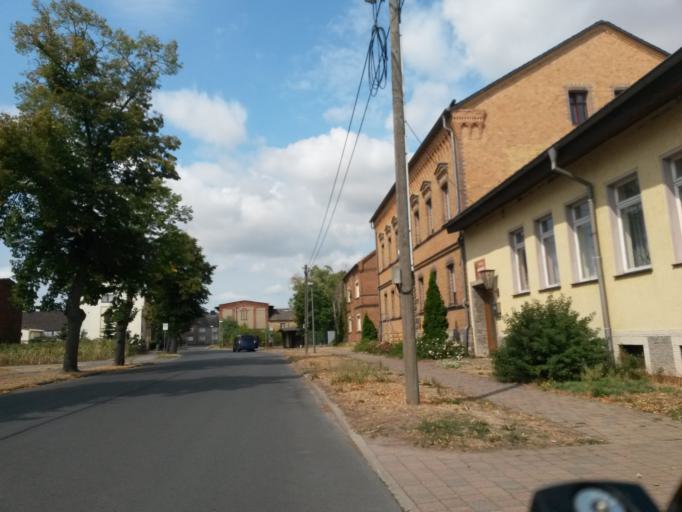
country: DE
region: Saxony-Anhalt
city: Muhlanger
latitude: 51.8232
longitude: 12.7238
